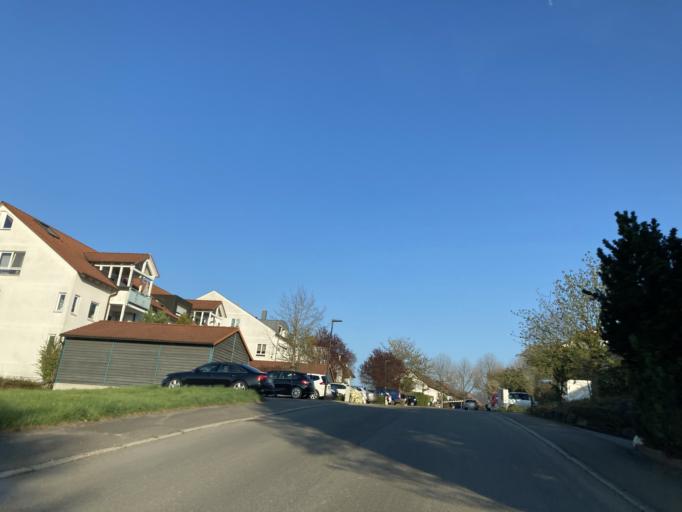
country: DE
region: Baden-Wuerttemberg
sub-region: Tuebingen Region
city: Nehren
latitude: 48.4354
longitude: 9.0690
